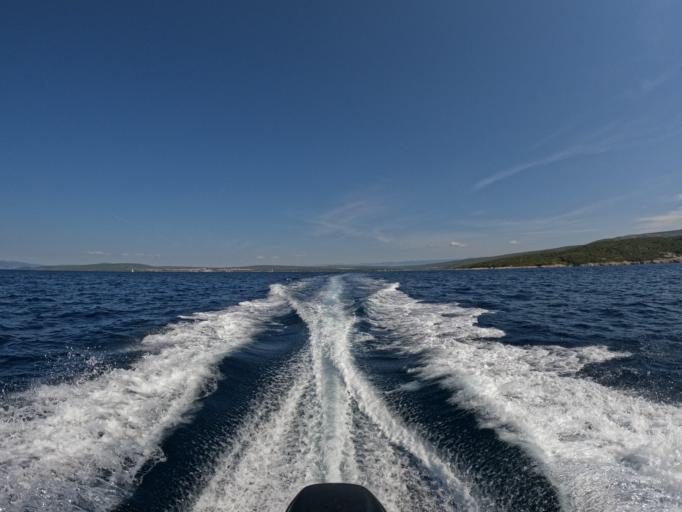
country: HR
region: Primorsko-Goranska
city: Punat
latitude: 44.9725
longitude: 14.6088
